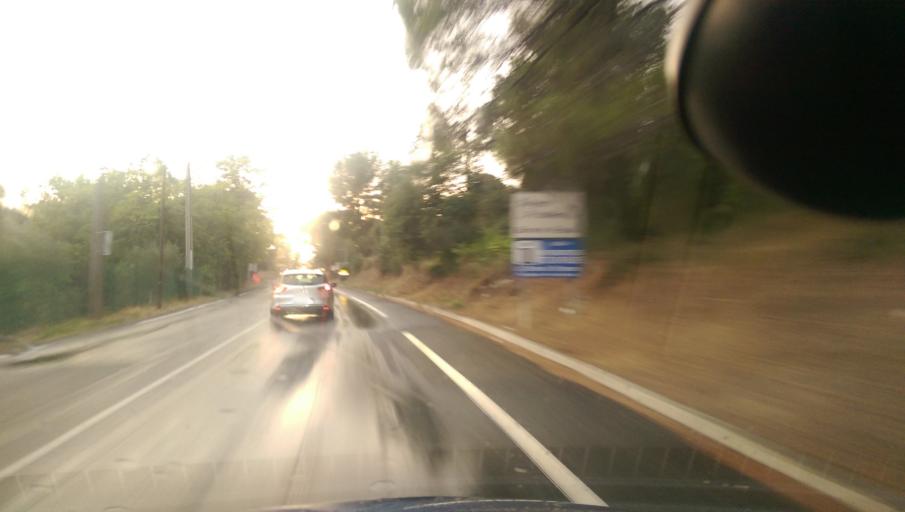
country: FR
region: Provence-Alpes-Cote d'Azur
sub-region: Departement des Alpes-Maritimes
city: Grasse
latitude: 43.6681
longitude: 6.9234
